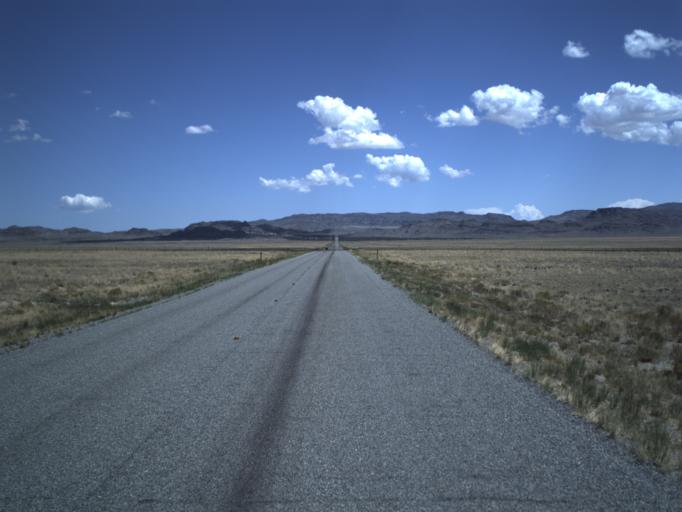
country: US
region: Utah
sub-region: Beaver County
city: Milford
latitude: 39.0453
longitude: -113.7988
